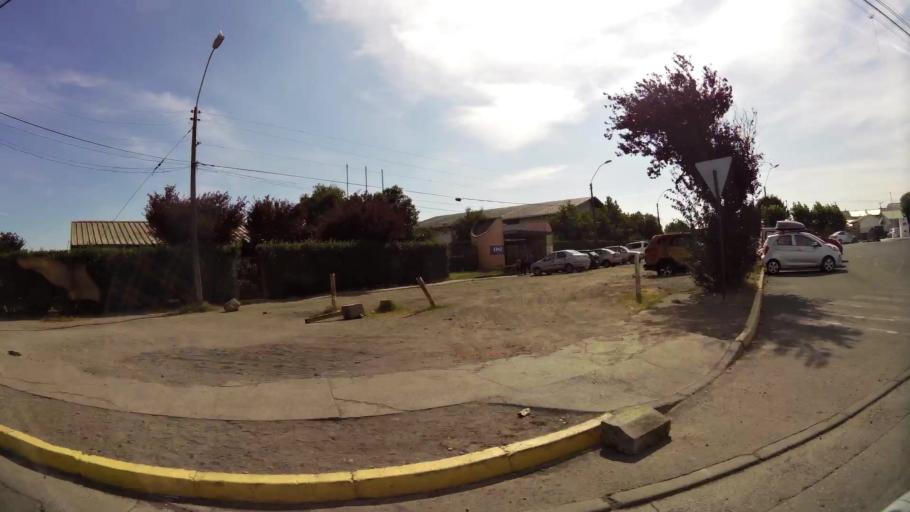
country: CL
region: Biobio
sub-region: Provincia de Concepcion
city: Talcahuano
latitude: -36.7825
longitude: -73.1029
